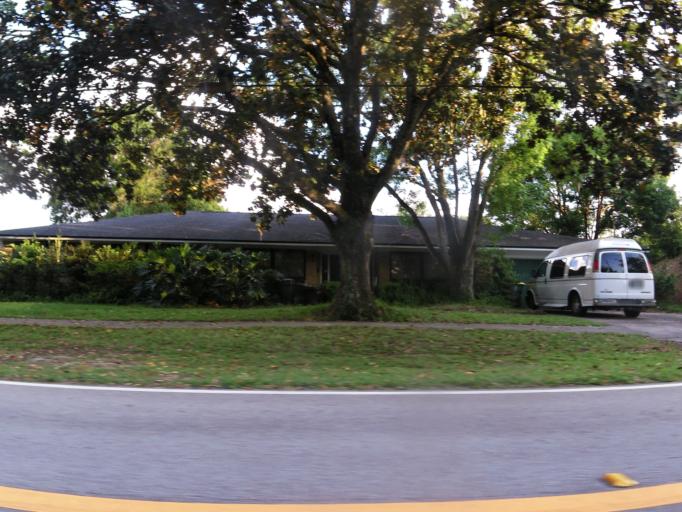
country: US
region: Florida
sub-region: Clay County
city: Orange Park
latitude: 30.2257
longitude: -81.6120
